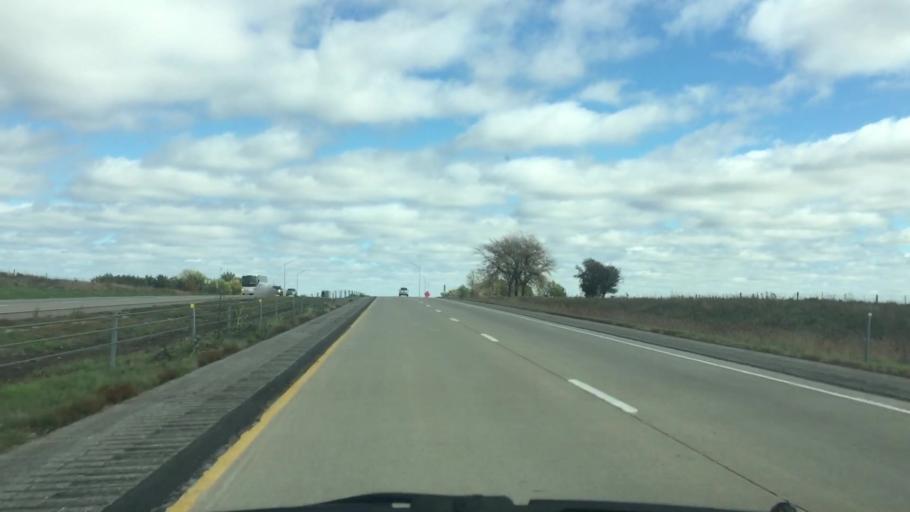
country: US
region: Iowa
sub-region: Iowa County
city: Marengo
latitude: 41.6957
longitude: -92.2396
